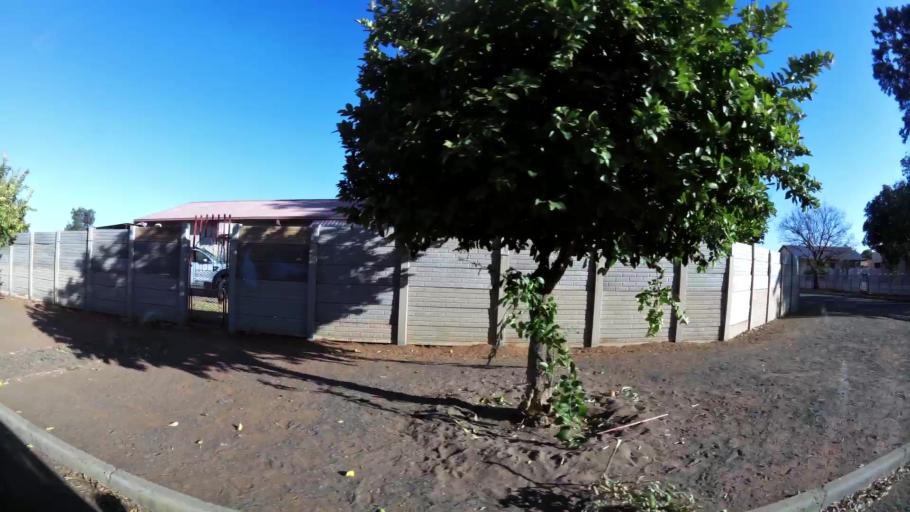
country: ZA
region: Northern Cape
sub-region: Frances Baard District Municipality
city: Kimberley
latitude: -28.7404
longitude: 24.7389
